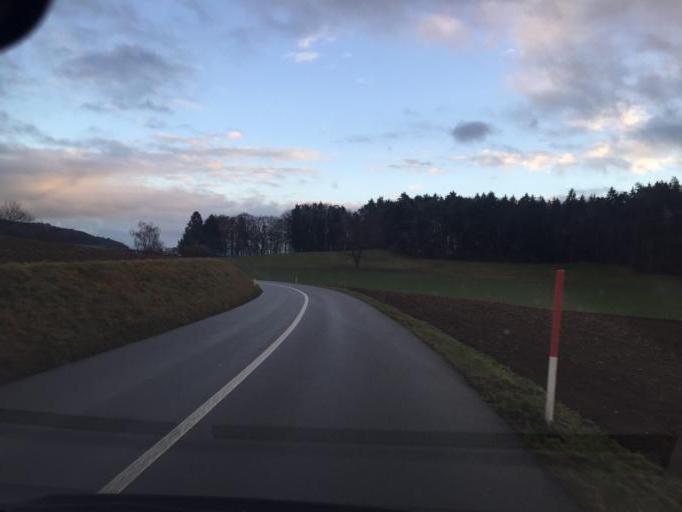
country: DE
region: Baden-Wuerttemberg
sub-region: Freiburg Region
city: Busingen
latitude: 47.7143
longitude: 8.7050
